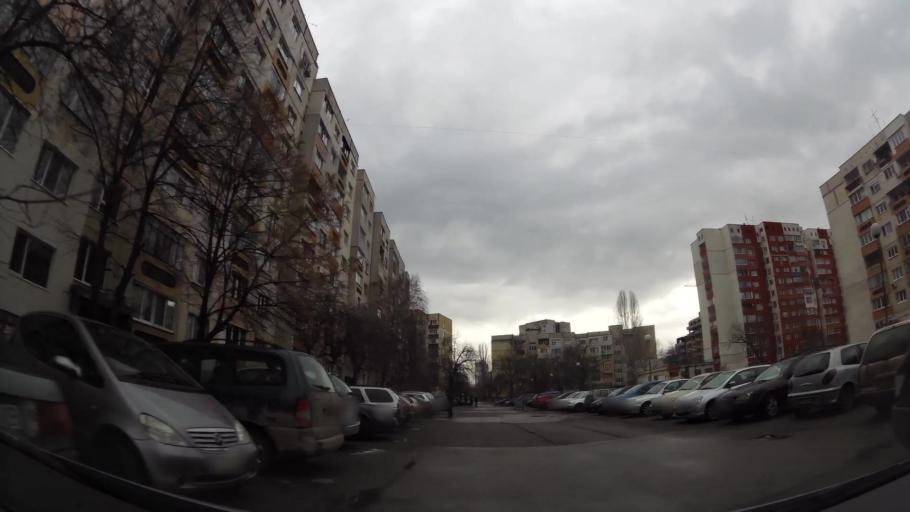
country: BG
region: Sofia-Capital
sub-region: Stolichna Obshtina
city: Sofia
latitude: 42.7288
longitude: 23.2979
